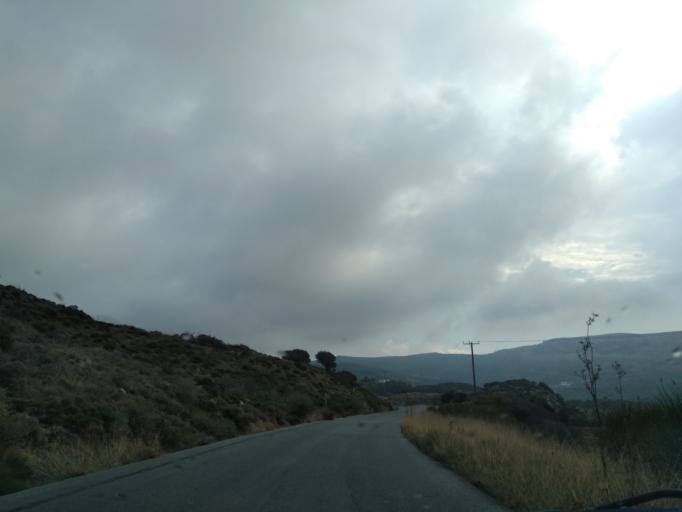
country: GR
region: Crete
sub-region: Nomos Lasithiou
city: Siteia
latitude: 35.1526
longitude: 26.0187
